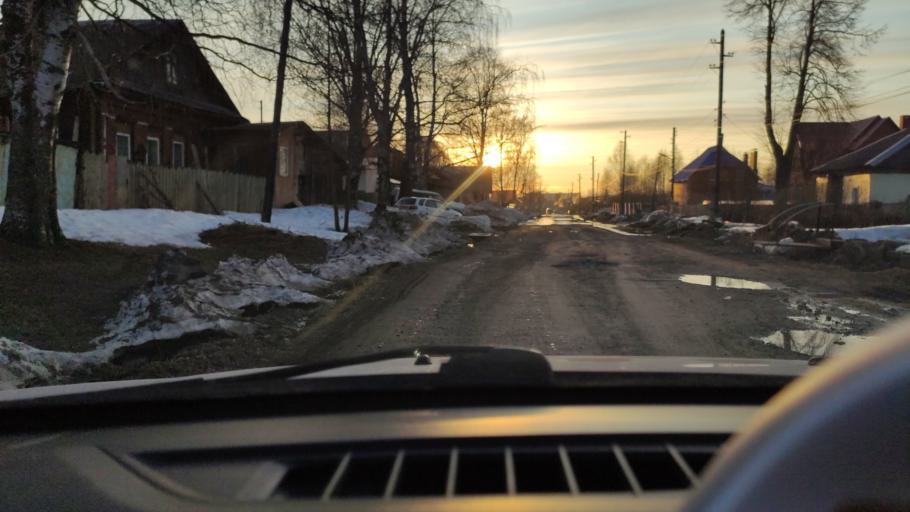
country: RU
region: Perm
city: Polazna
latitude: 58.1166
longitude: 56.4064
